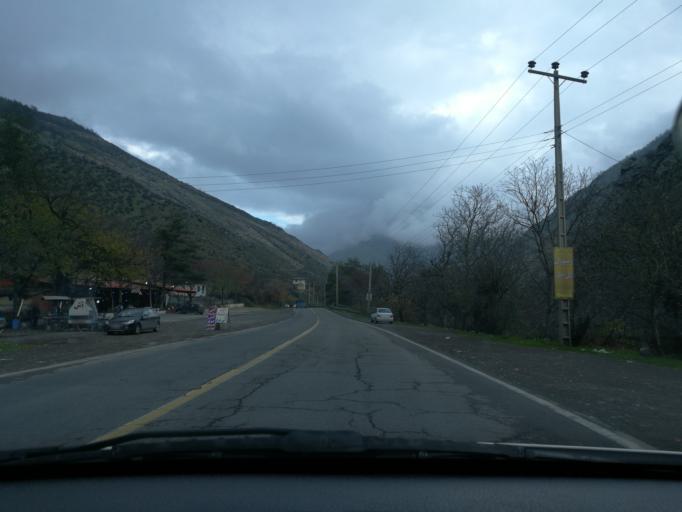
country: IR
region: Mazandaran
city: Chalus
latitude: 36.3665
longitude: 51.2627
